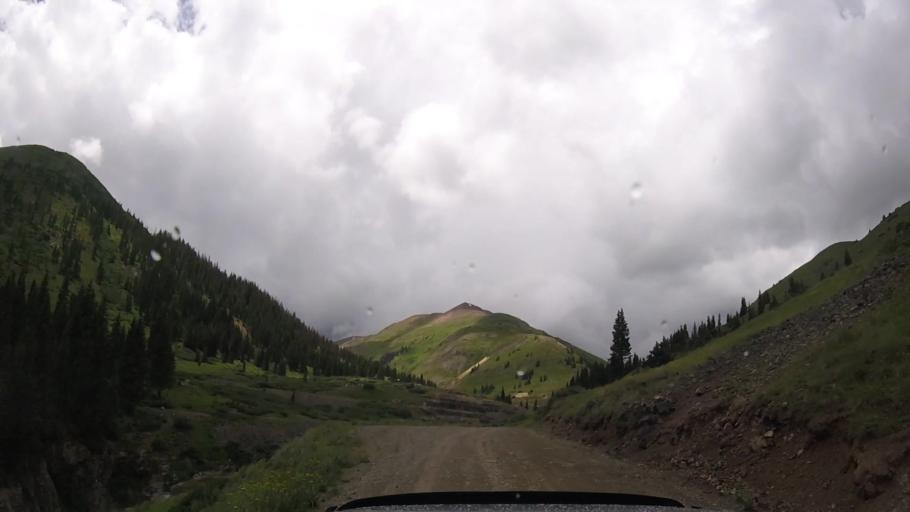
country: US
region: Colorado
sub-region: Ouray County
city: Ouray
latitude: 37.9290
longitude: -107.5663
